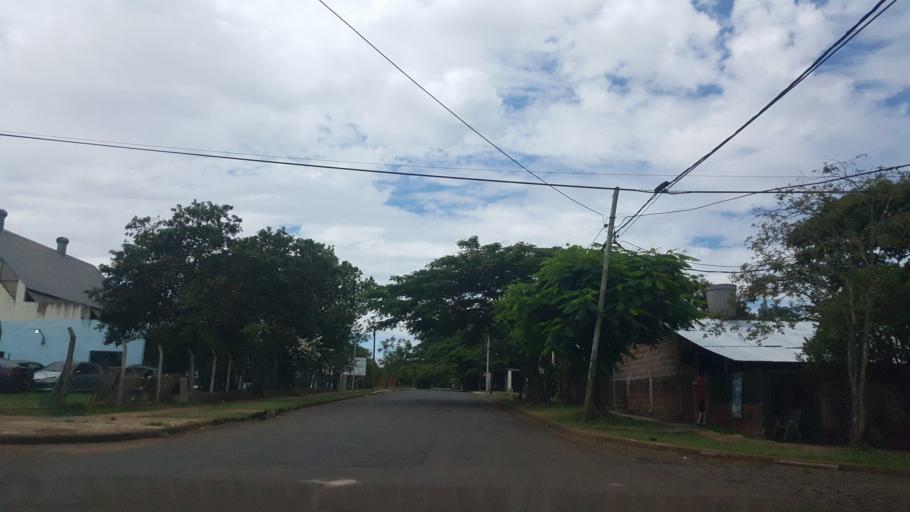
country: AR
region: Misiones
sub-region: Departamento de Capital
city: Posadas
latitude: -27.4208
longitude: -55.8862
